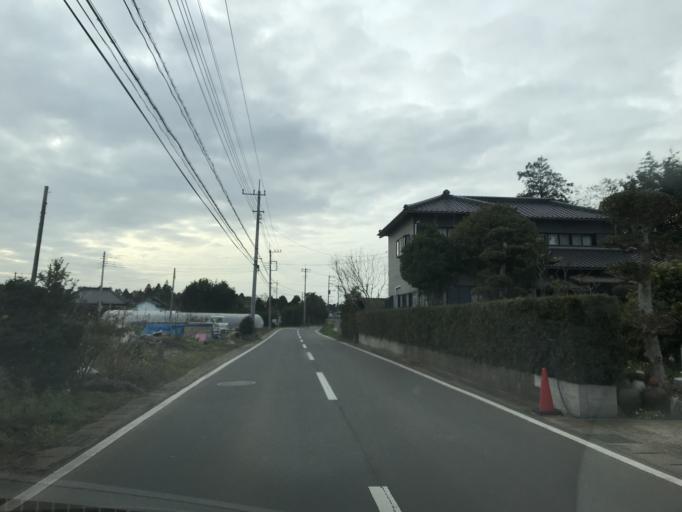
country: JP
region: Chiba
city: Omigawa
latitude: 35.7995
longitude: 140.5808
